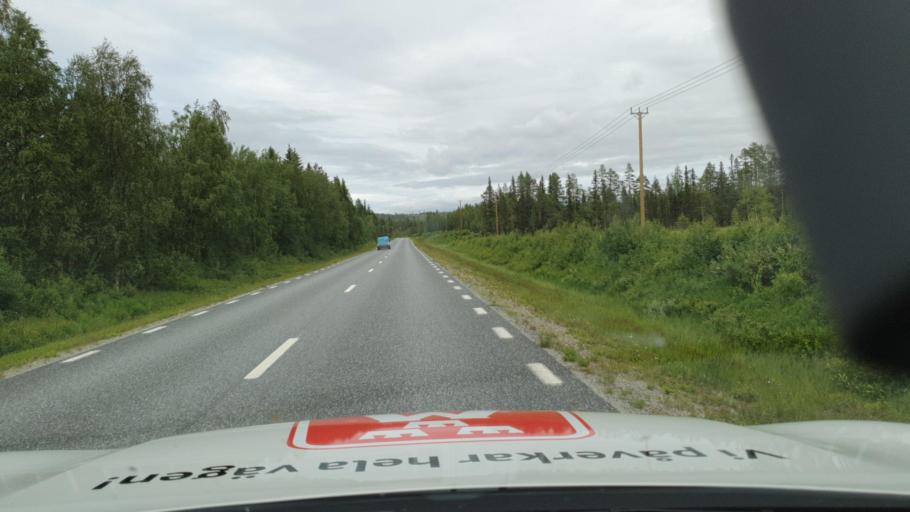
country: SE
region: Vaesterbotten
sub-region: Asele Kommun
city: Insjon
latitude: 64.3121
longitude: 17.6968
